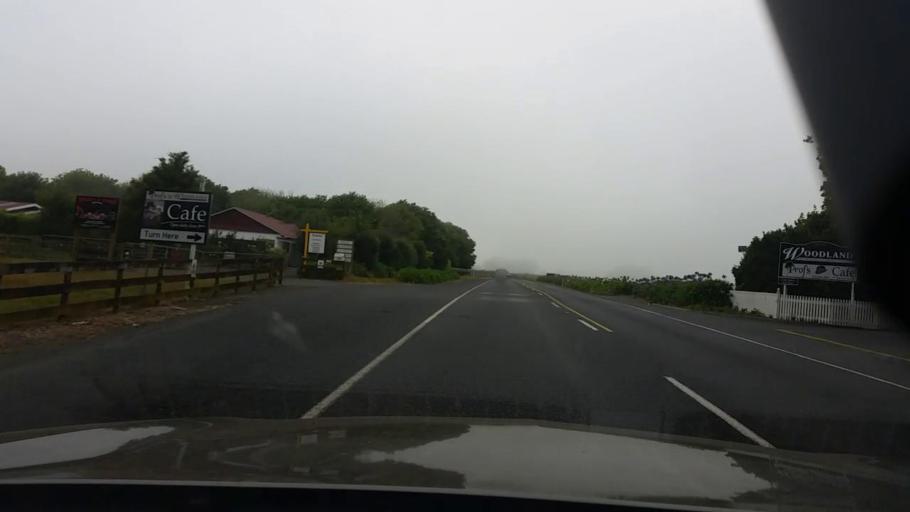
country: NZ
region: Waikato
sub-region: Hamilton City
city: Hamilton
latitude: -37.6532
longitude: 175.2956
